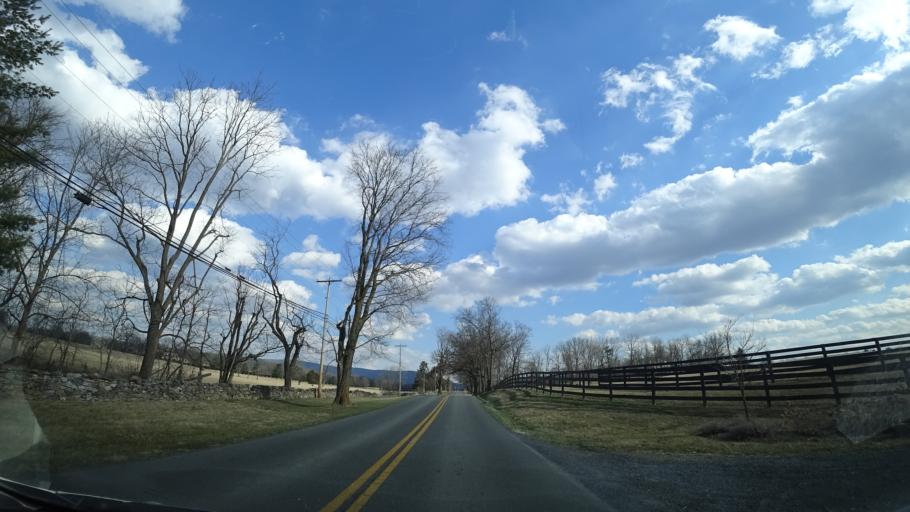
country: US
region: Virginia
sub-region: Warren County
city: Shenandoah Farms
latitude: 39.0599
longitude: -78.0246
